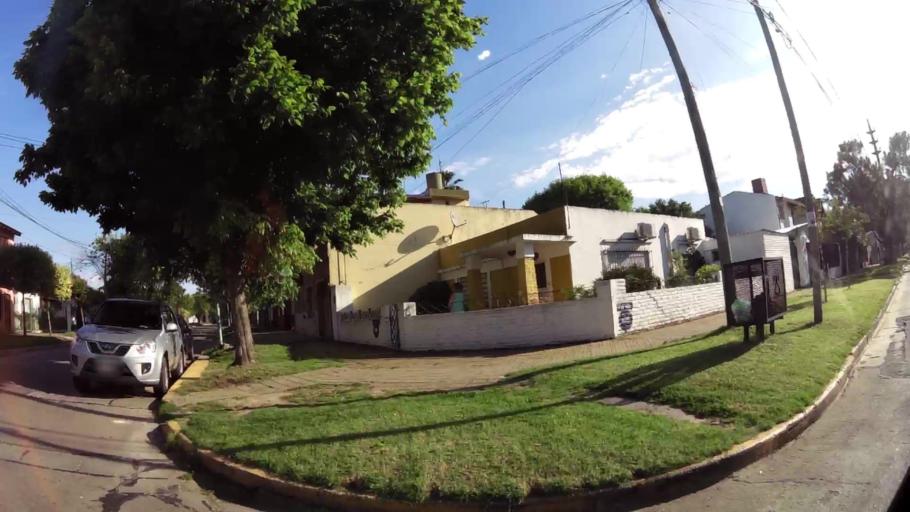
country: AR
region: Buenos Aires
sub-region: Partido de Merlo
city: Merlo
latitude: -34.6698
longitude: -58.7327
